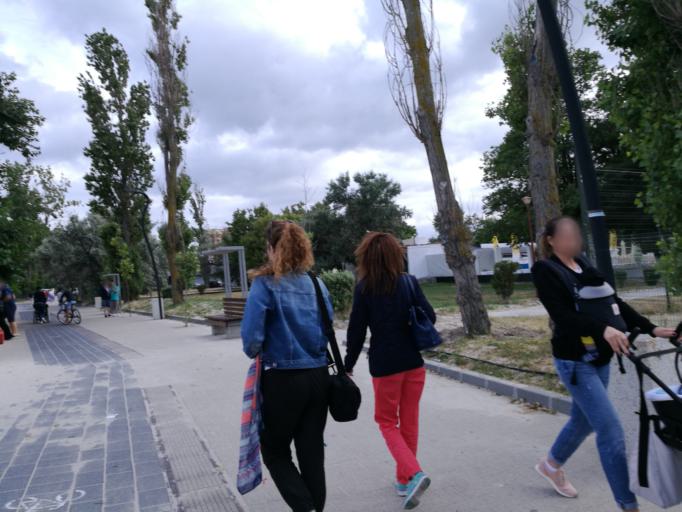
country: RO
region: Constanta
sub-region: Municipiul Constanta
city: Palazu Mare
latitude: 44.2498
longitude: 28.6219
